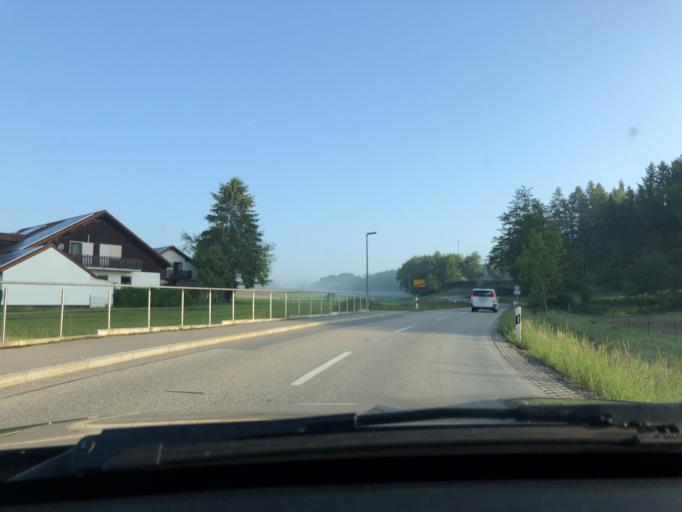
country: DE
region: Bavaria
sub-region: Upper Bavaria
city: Kirchdorf
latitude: 48.4607
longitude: 11.6490
